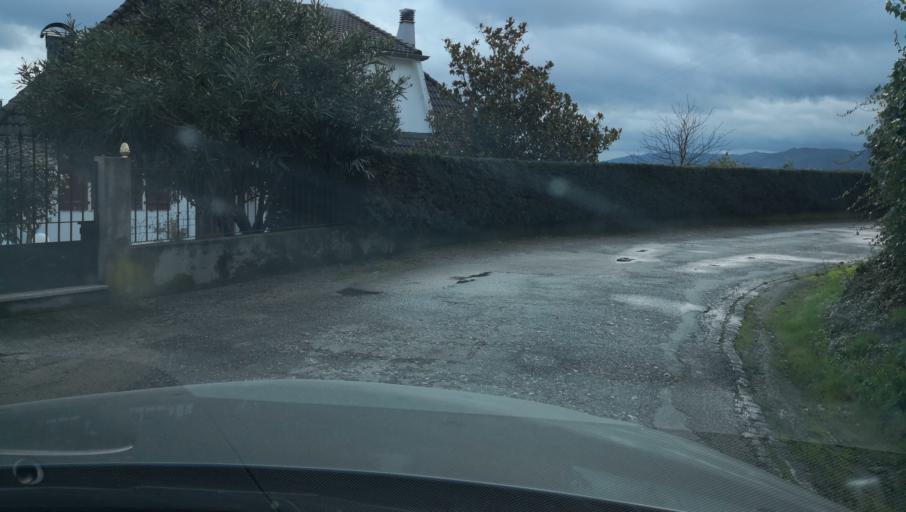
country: PT
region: Vila Real
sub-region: Sabrosa
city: Vilela
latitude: 41.1920
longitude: -7.5686
